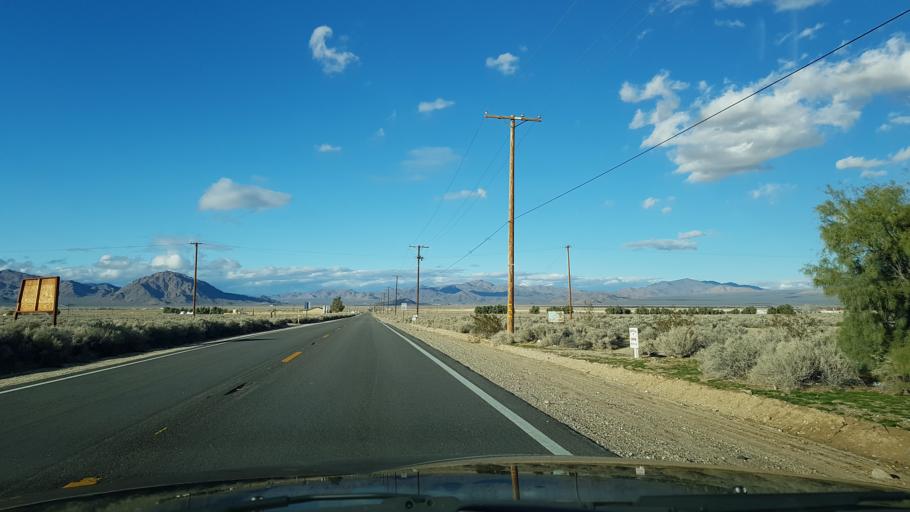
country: US
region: California
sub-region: San Bernardino County
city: Lucerne Valley
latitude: 34.4500
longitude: -116.9458
